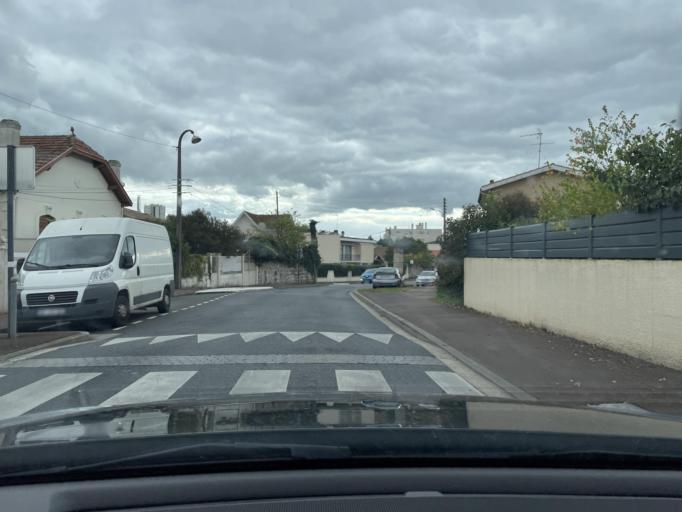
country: FR
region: Aquitaine
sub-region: Departement de la Gironde
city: Le Bouscat
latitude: 44.8669
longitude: -0.5904
